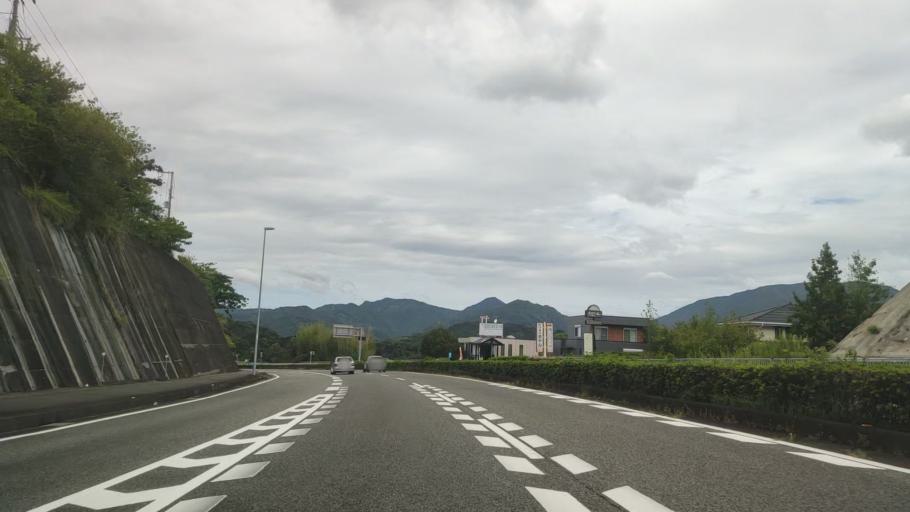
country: JP
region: Wakayama
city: Tanabe
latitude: 33.7337
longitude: 135.4007
